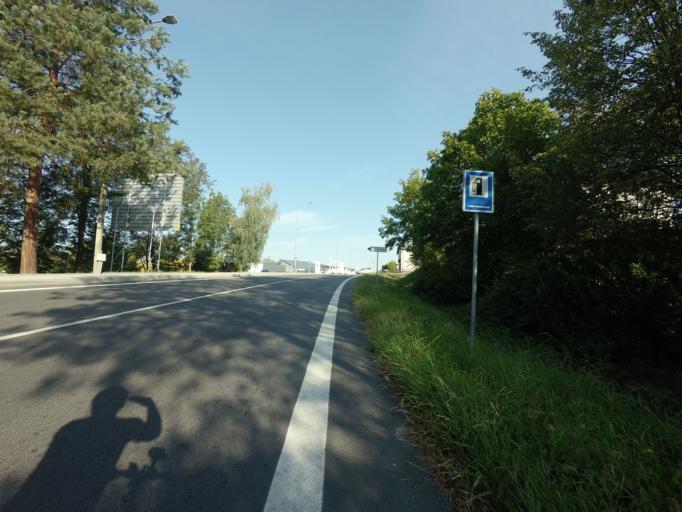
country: CZ
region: Jihocesky
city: Tyn nad Vltavou
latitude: 49.2285
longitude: 14.4235
